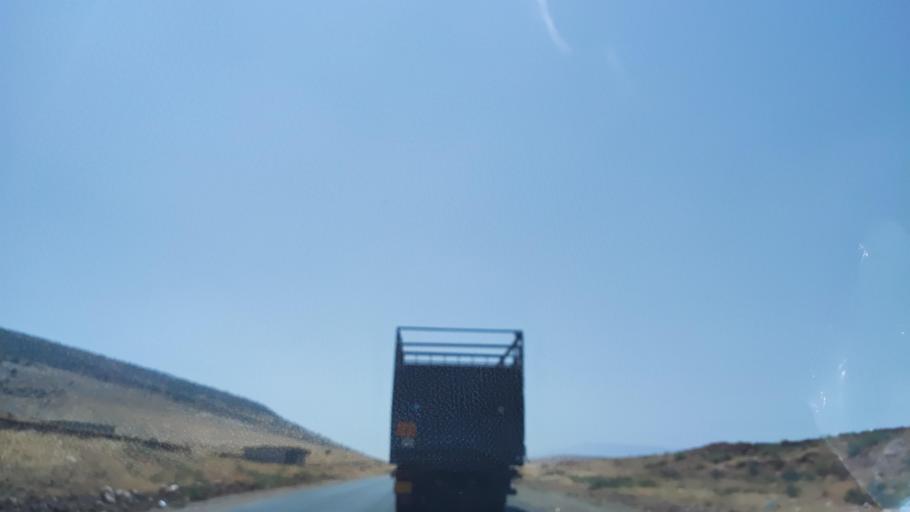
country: IQ
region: Arbil
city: Shaqlawah
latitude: 36.5964
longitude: 44.3175
